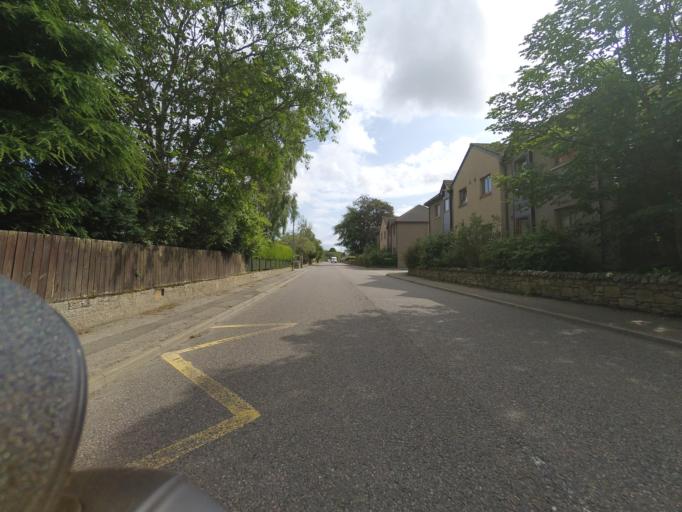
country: GB
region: Scotland
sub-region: Highland
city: Tain
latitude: 57.8085
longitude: -4.0508
